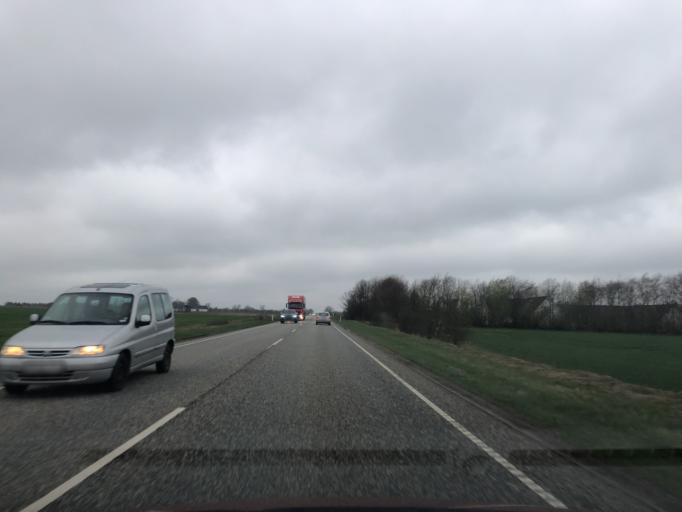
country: DK
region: Central Jutland
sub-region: Holstebro Kommune
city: Holstebro
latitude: 56.3147
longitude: 8.6882
